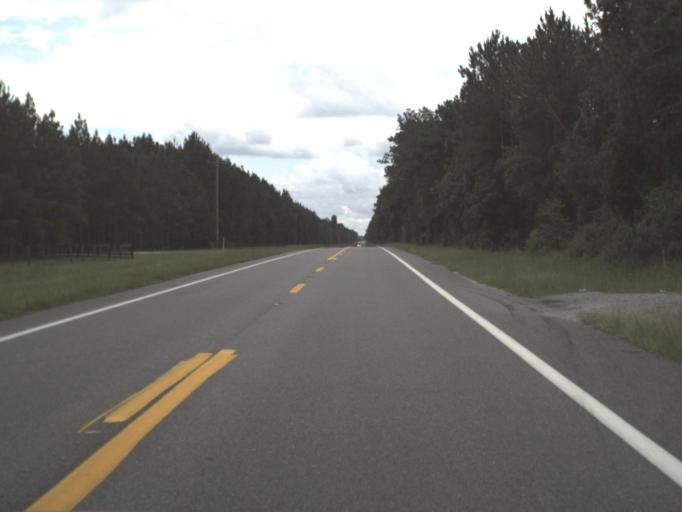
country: US
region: Florida
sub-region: Union County
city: Lake Butler
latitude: 30.0484
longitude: -82.3997
